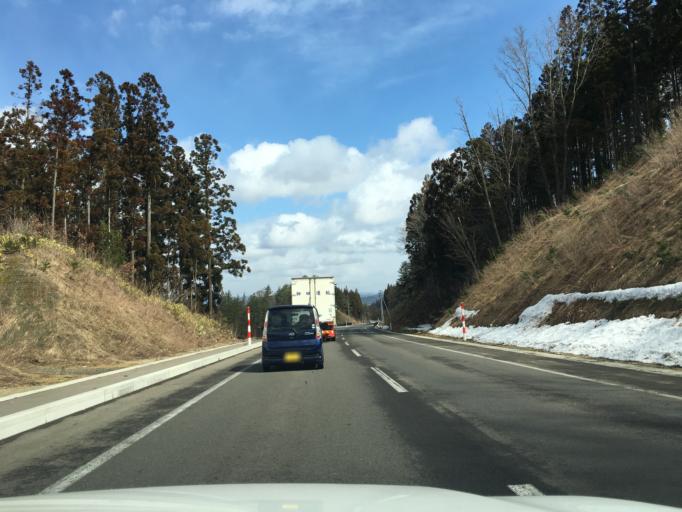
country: JP
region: Akita
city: Takanosu
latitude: 40.1062
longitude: 140.3518
